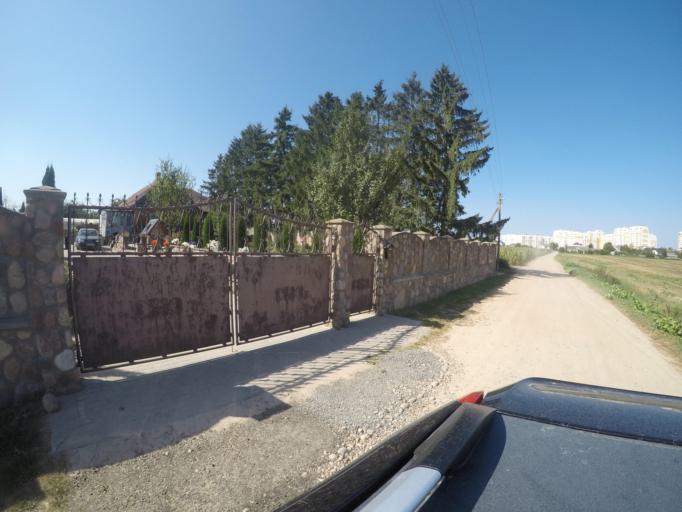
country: BY
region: Grodnenskaya
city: Hrodna
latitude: 53.7092
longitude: 23.8735
